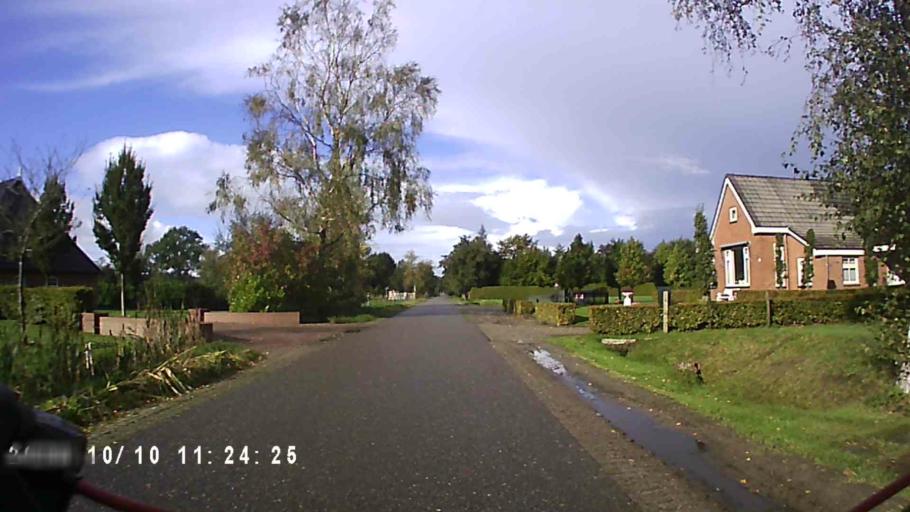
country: NL
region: Friesland
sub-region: Gemeente Smallingerland
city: Drachtstercompagnie
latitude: 53.0875
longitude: 6.1749
